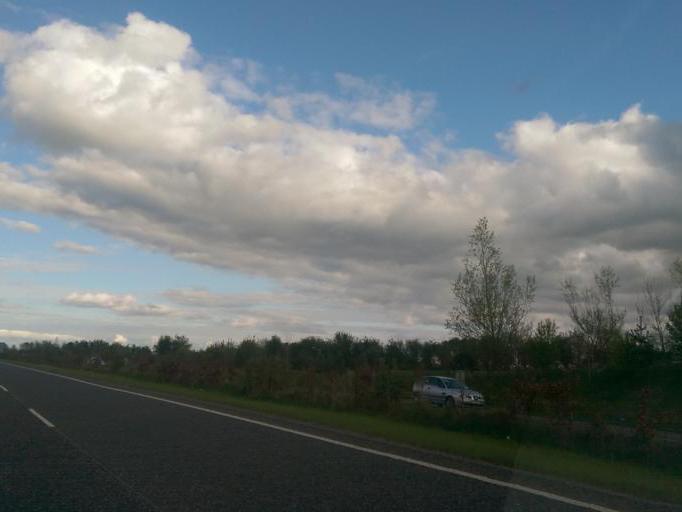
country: IE
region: Leinster
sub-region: An Iarmhi
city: Kinnegad
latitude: 53.4476
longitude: -7.0832
